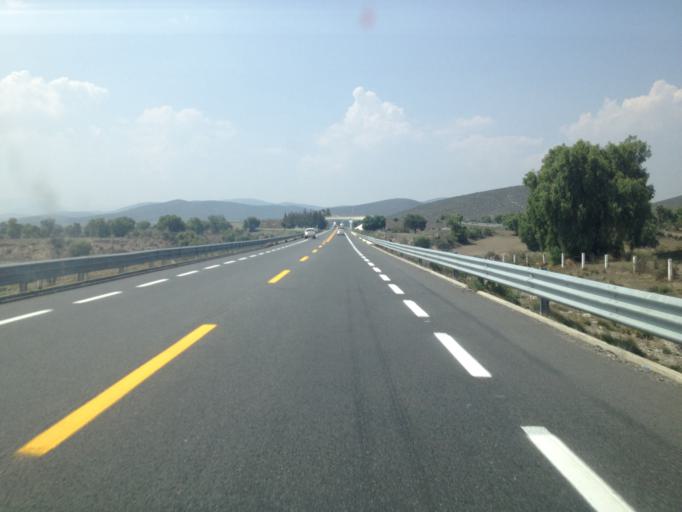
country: MX
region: Puebla
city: Cuacnopalan
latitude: 18.8099
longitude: -97.4905
